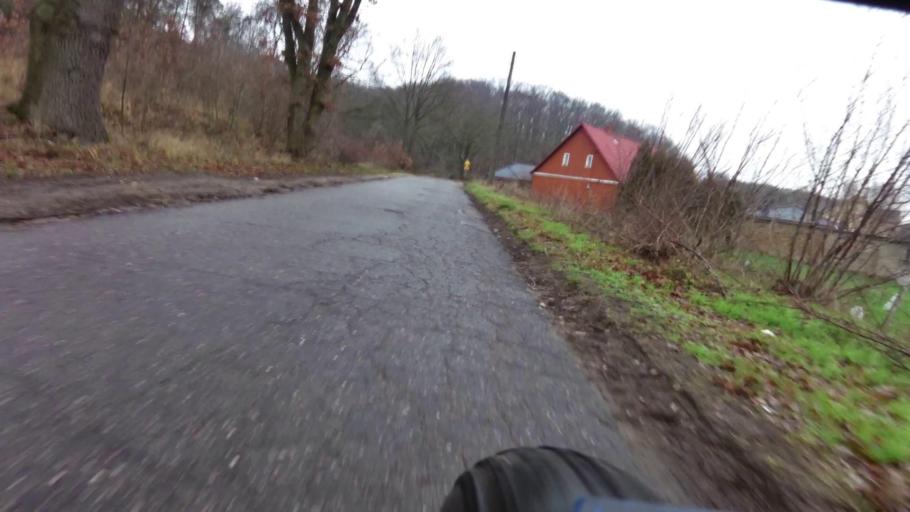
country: PL
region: Lubusz
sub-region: Powiat gorzowski
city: Kostrzyn nad Odra
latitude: 52.6232
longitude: 14.7106
